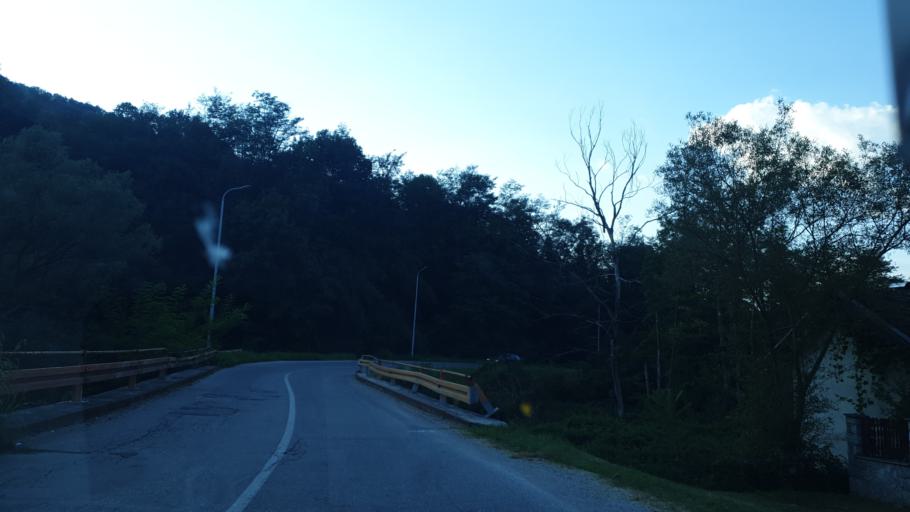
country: RS
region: Central Serbia
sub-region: Zlatiborski Okrug
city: Pozega
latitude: 43.9165
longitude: 20.0057
